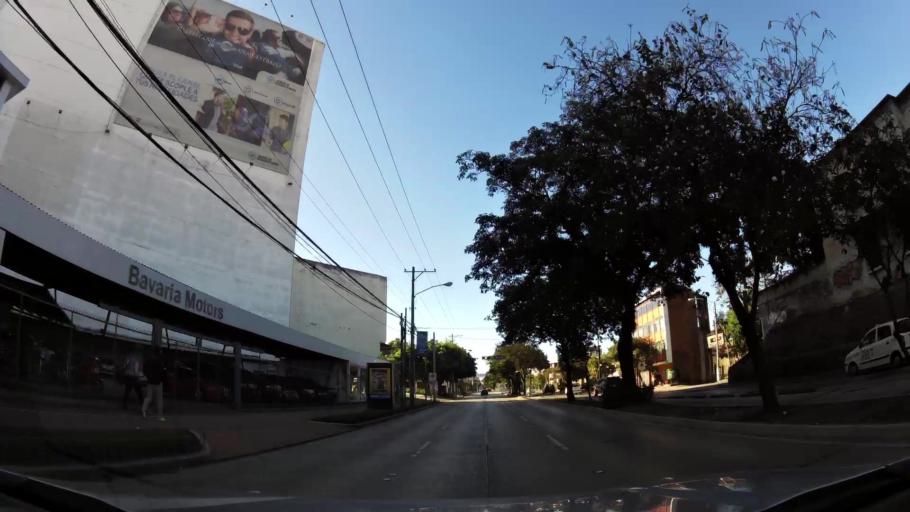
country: GT
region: Guatemala
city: Guatemala City
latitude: 14.6182
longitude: -90.5173
